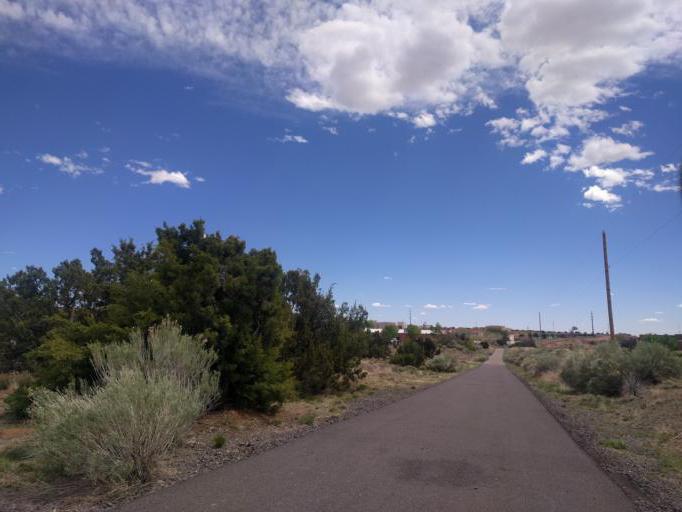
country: US
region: New Mexico
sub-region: Santa Fe County
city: Santa Fe
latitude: 35.6385
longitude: -105.9634
